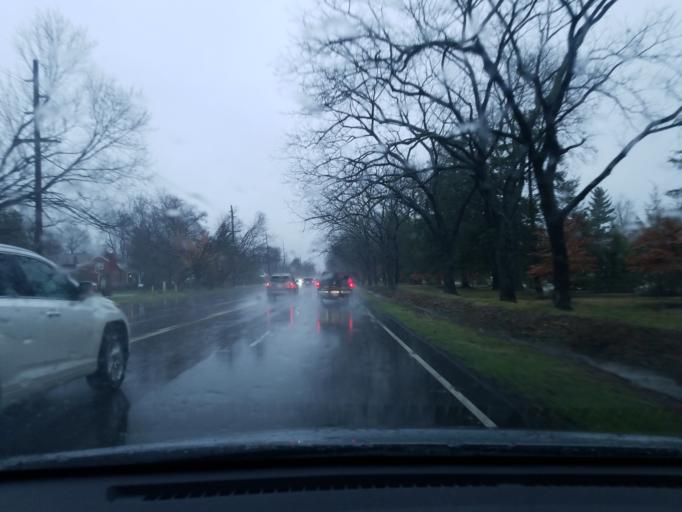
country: US
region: Kentucky
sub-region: Jefferson County
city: Lyndon
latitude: 38.2480
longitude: -85.5970
